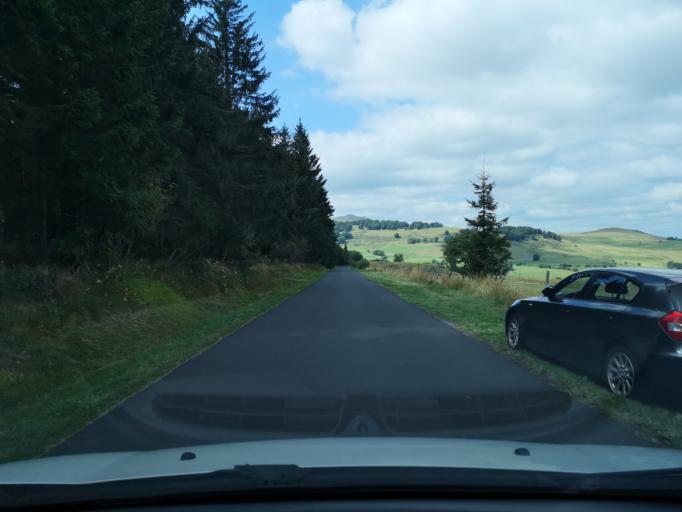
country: FR
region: Auvergne
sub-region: Departement du Puy-de-Dome
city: Mont-Dore
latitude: 45.4970
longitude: 2.8934
